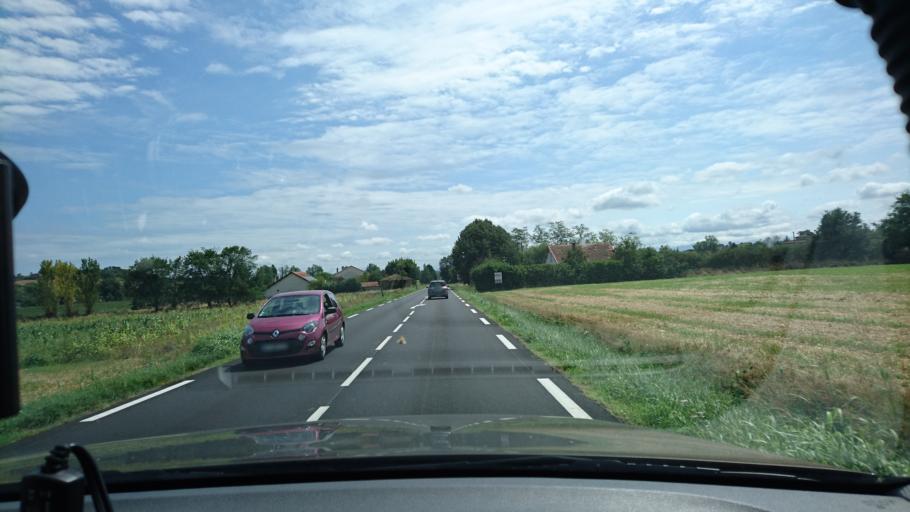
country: FR
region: Midi-Pyrenees
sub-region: Departement de la Haute-Garonne
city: Gaillac-Toulza
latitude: 43.1829
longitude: 1.4018
